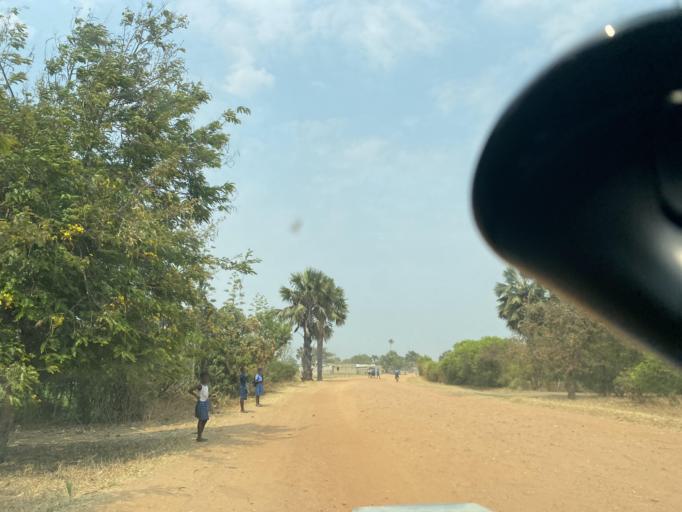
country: ZM
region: Lusaka
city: Kafue
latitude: -15.6606
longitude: 28.0248
